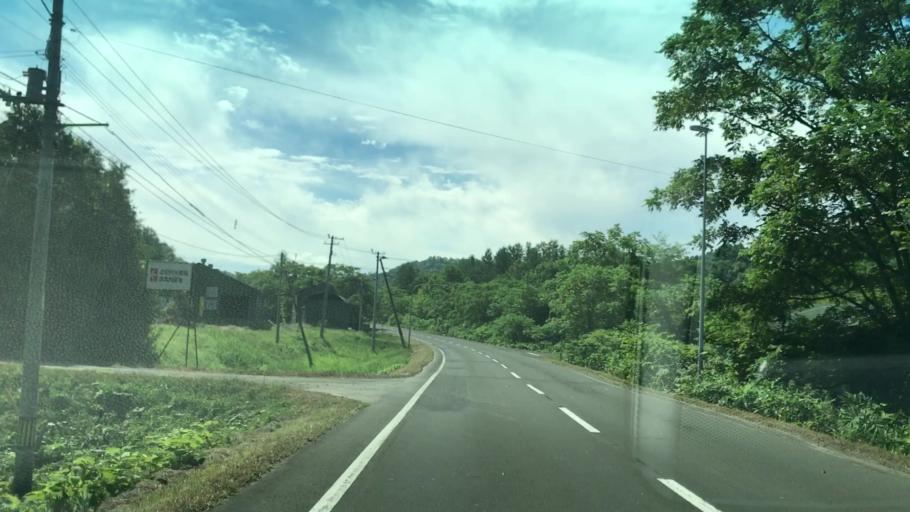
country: JP
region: Hokkaido
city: Shimo-furano
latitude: 42.9598
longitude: 142.4285
